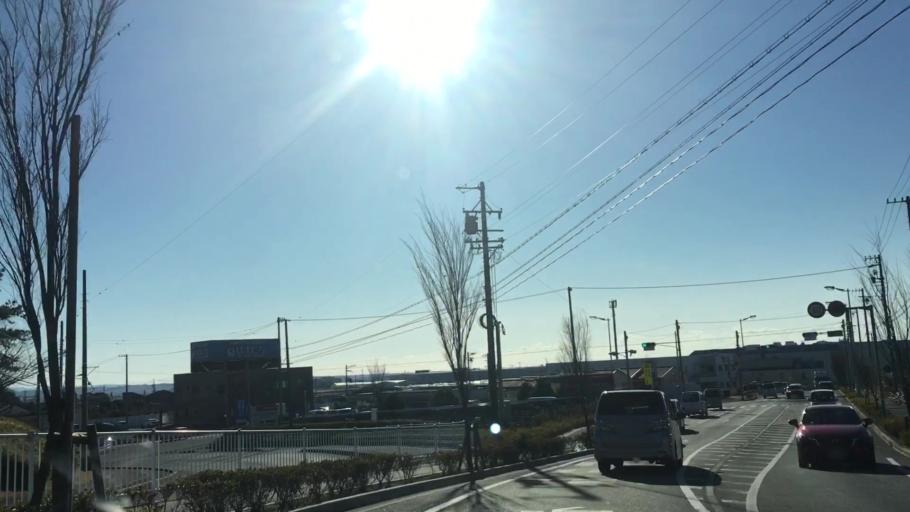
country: JP
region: Shizuoka
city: Hamakita
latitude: 34.8010
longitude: 137.7461
